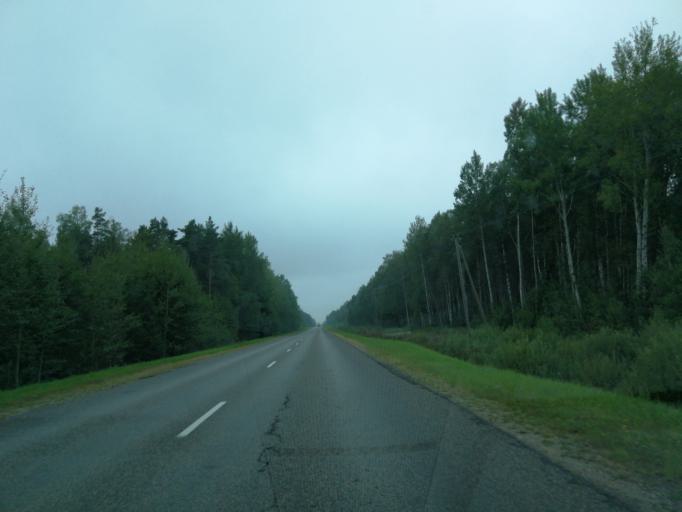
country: LV
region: Varkava
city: Vecvarkava
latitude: 56.3211
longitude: 26.4292
